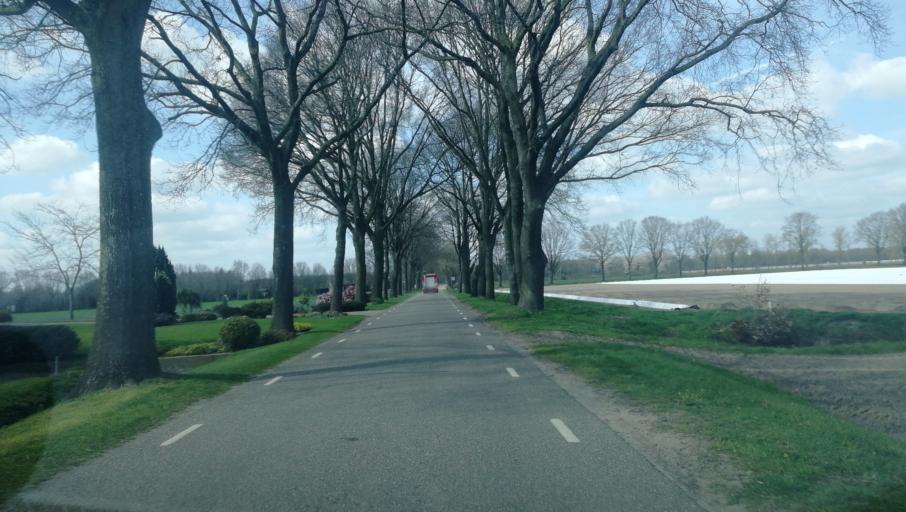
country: NL
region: Limburg
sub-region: Gemeente Beesel
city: Beesel
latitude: 51.2866
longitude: 6.0119
